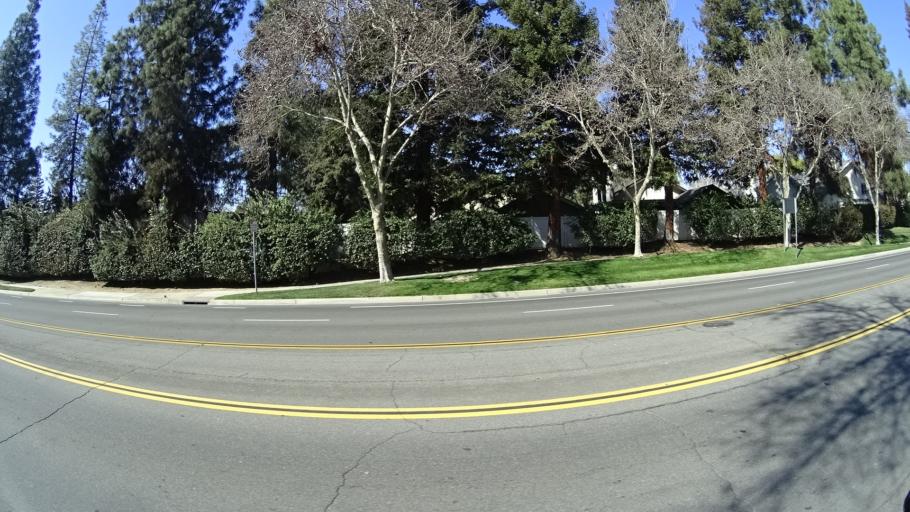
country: US
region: California
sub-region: Fresno County
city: Clovis
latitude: 36.8672
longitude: -119.7702
